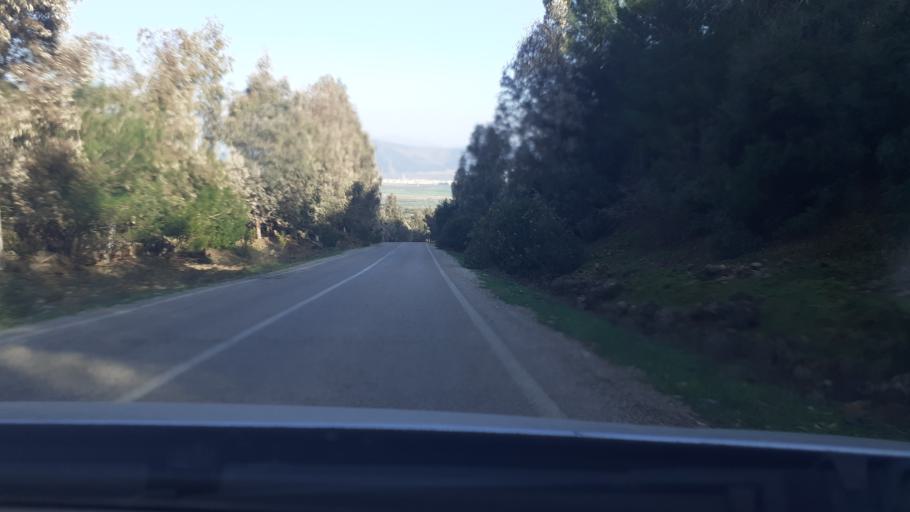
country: TR
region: Hatay
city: Aktepe
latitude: 36.7327
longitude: 36.4753
